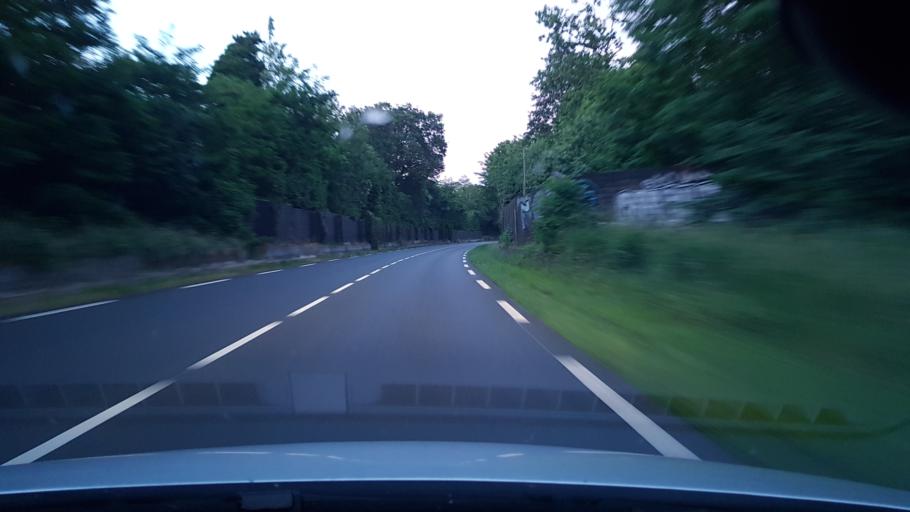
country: FR
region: Ile-de-France
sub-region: Departement de l'Essonne
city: Orsay
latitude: 48.6966
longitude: 2.2097
